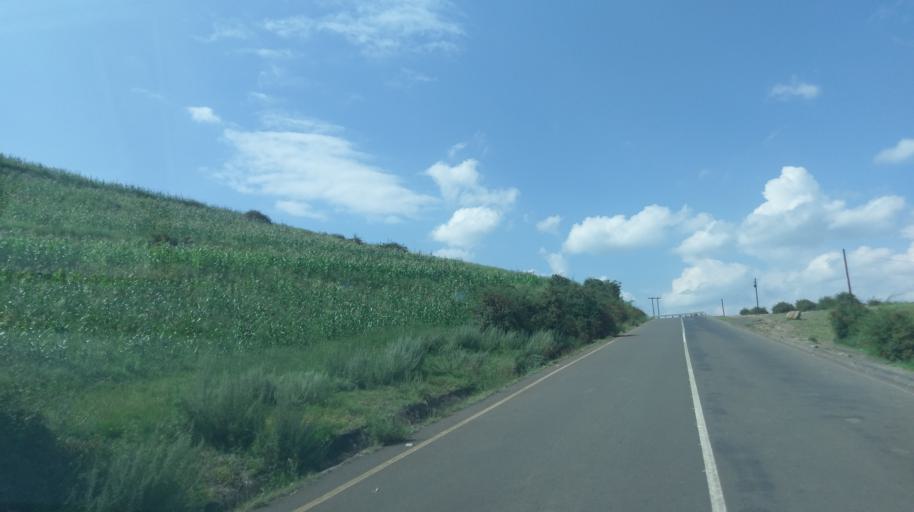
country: LS
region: Thaba-Tseka
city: Thaba-Tseka
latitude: -29.1220
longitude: 28.4922
